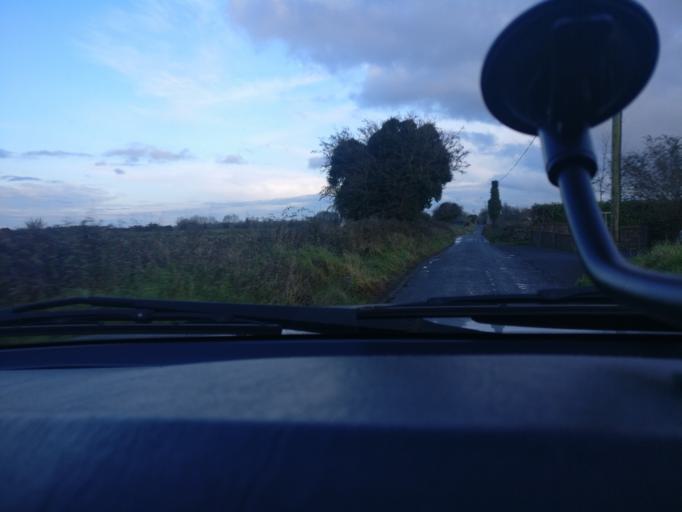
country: IE
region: Connaught
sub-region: County Galway
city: Loughrea
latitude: 53.1991
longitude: -8.6713
